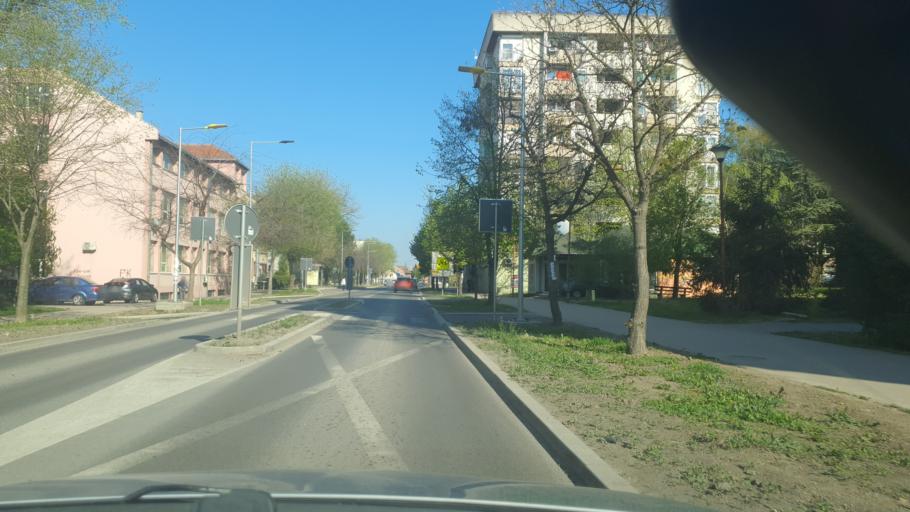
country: RS
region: Autonomna Pokrajina Vojvodina
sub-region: Zapadnobacki Okrug
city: Kula
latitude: 45.6114
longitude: 19.5295
